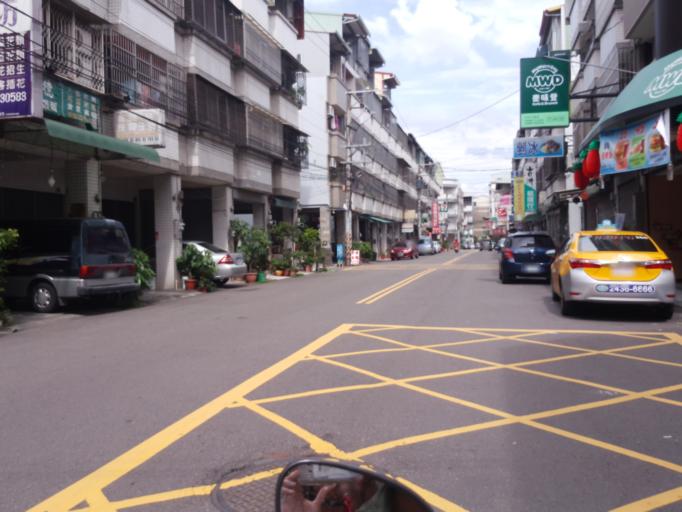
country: TW
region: Taiwan
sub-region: Taichung City
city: Taichung
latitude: 24.1094
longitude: 120.6926
